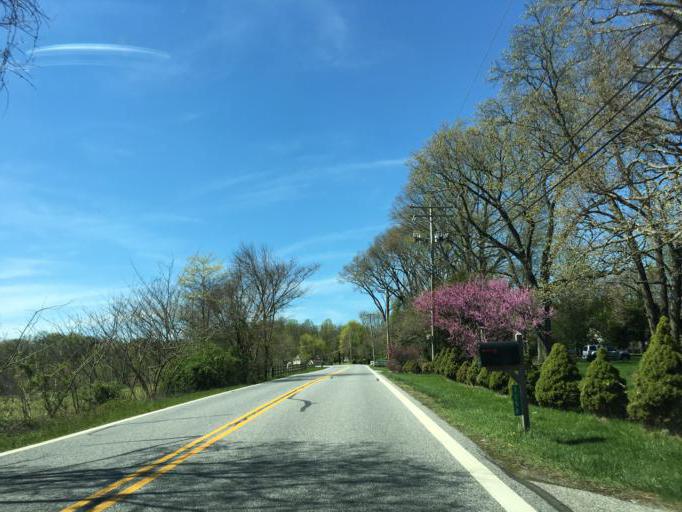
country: US
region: Maryland
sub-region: Baltimore County
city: Hunt Valley
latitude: 39.5901
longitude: -76.6373
